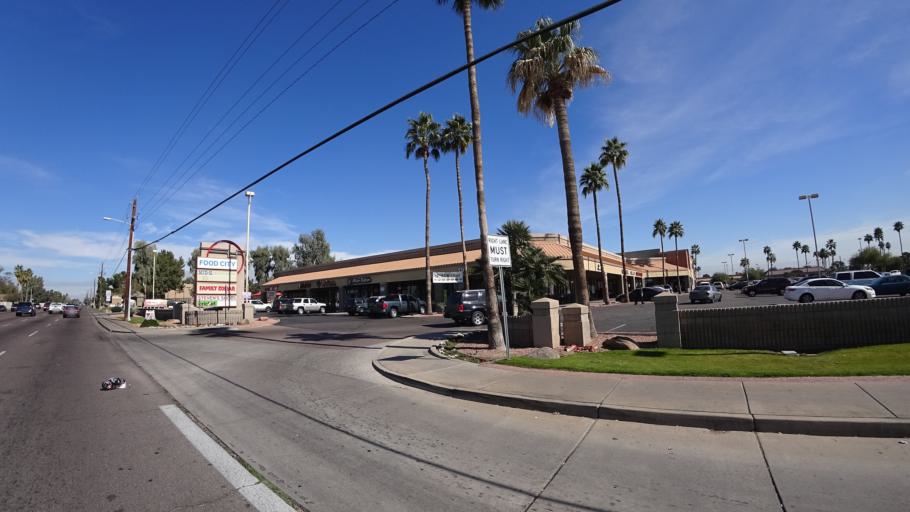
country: US
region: Arizona
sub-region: Maricopa County
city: Glendale
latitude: 33.4811
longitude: -112.2032
